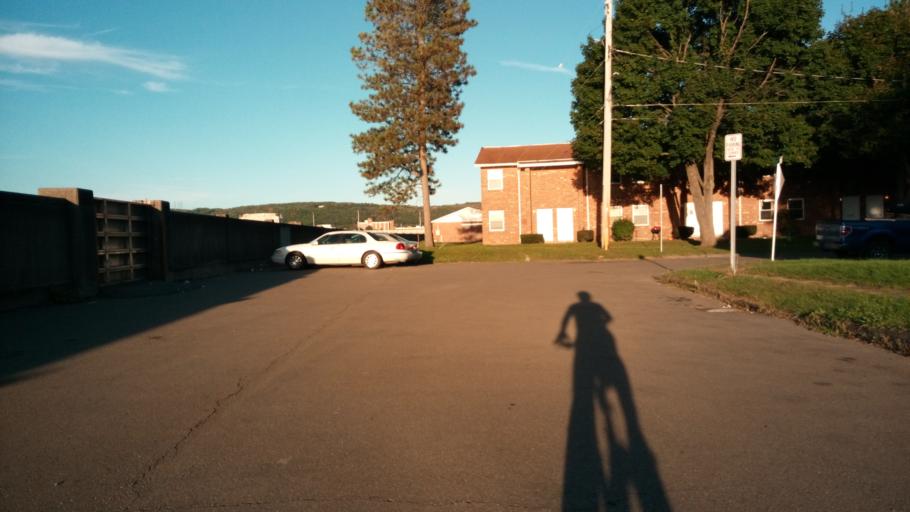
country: US
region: New York
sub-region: Chemung County
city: Elmira
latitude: 42.0841
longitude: -76.8099
